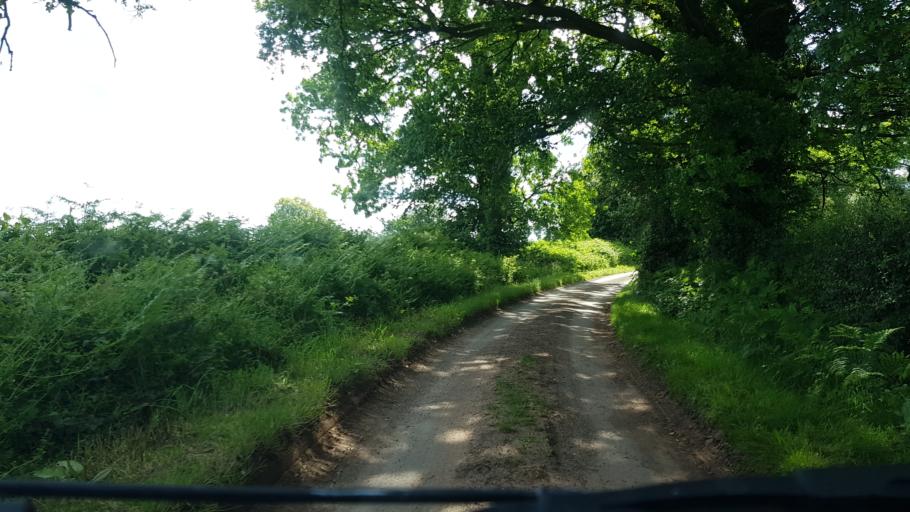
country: GB
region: England
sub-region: Shropshire
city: Romsley
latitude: 52.4612
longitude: -2.2869
